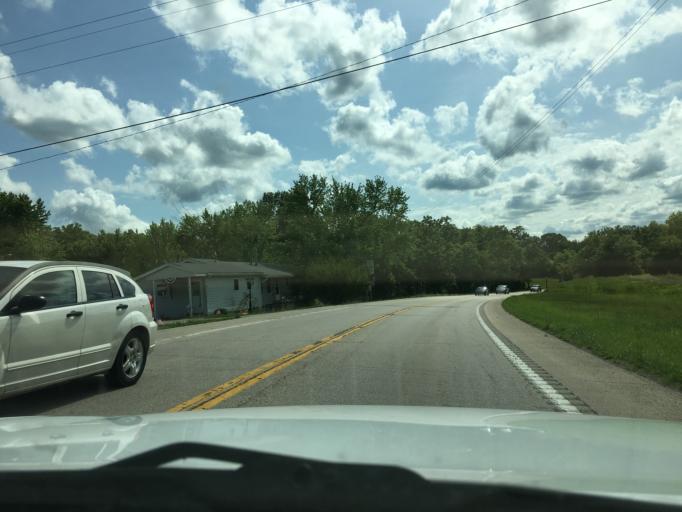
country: US
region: Missouri
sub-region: Franklin County
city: Gerald
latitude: 38.3951
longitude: -91.3409
